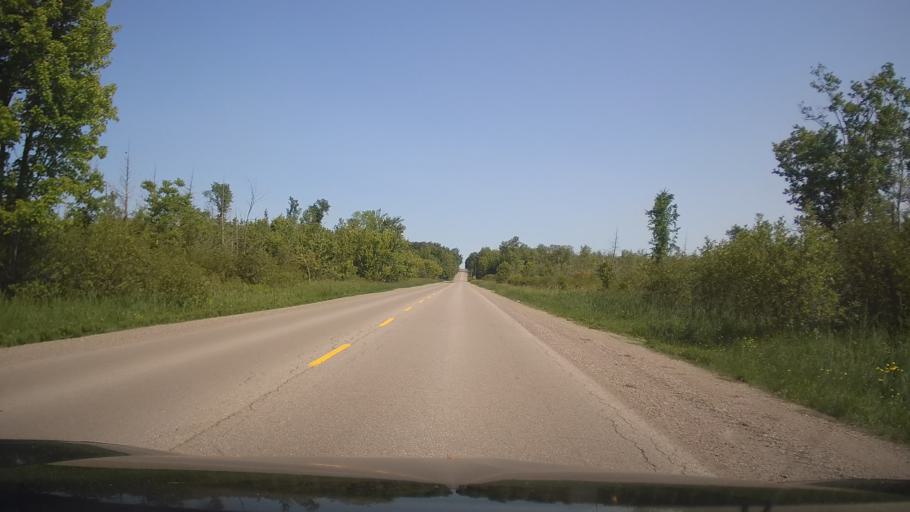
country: CA
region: Ontario
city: Uxbridge
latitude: 44.5206
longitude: -78.9604
